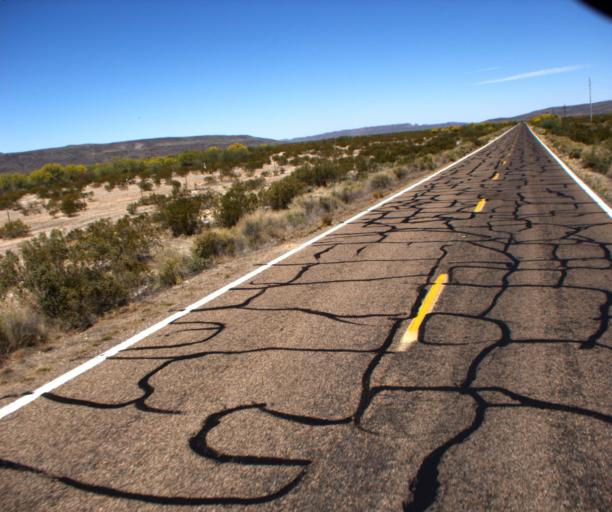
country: US
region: Arizona
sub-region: Pima County
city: Ajo
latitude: 32.4316
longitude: -112.8712
